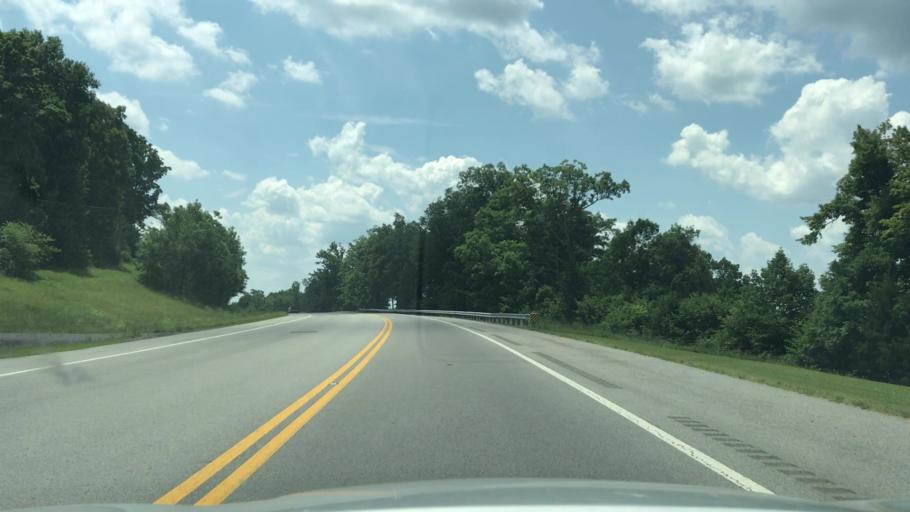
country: US
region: Tennessee
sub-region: Pickett County
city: Byrdstown
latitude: 36.5527
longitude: -85.1682
